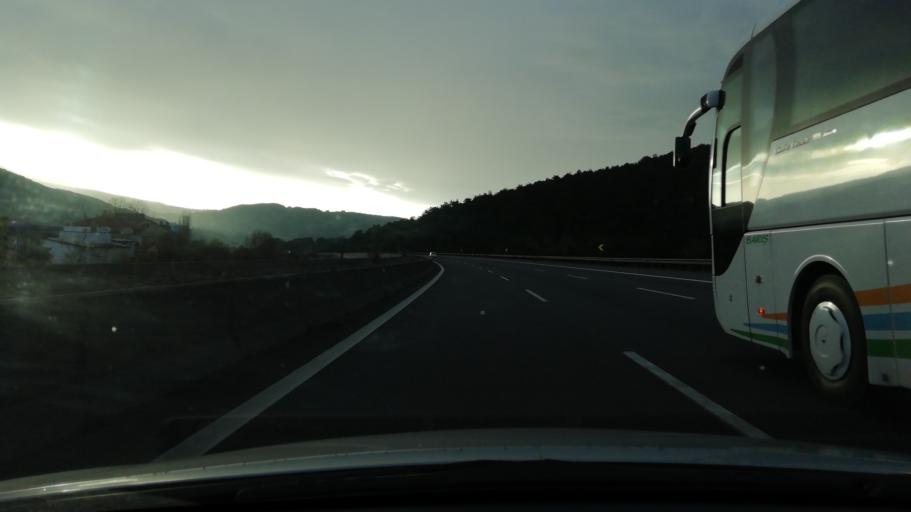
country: TR
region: Bolu
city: Gokcesu
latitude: 40.7395
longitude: 31.8265
